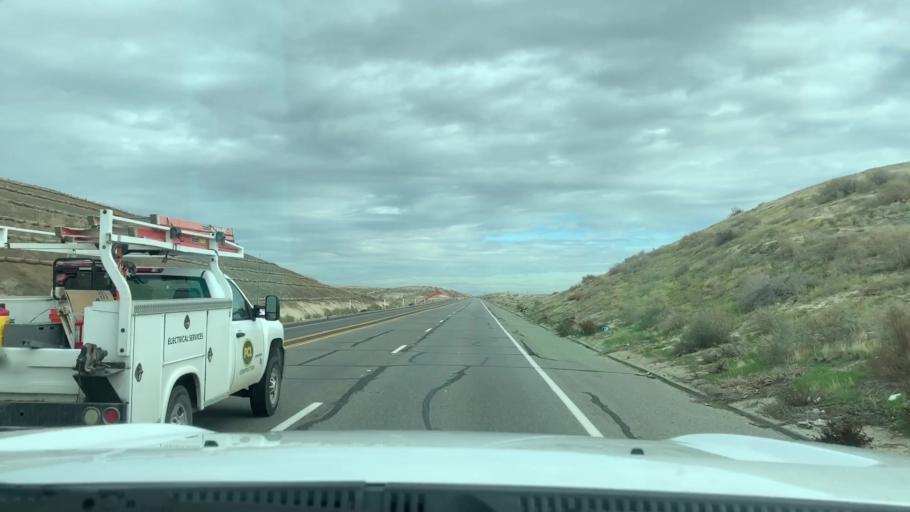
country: US
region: California
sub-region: Kern County
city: Ford City
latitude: 35.2430
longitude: -119.3524
